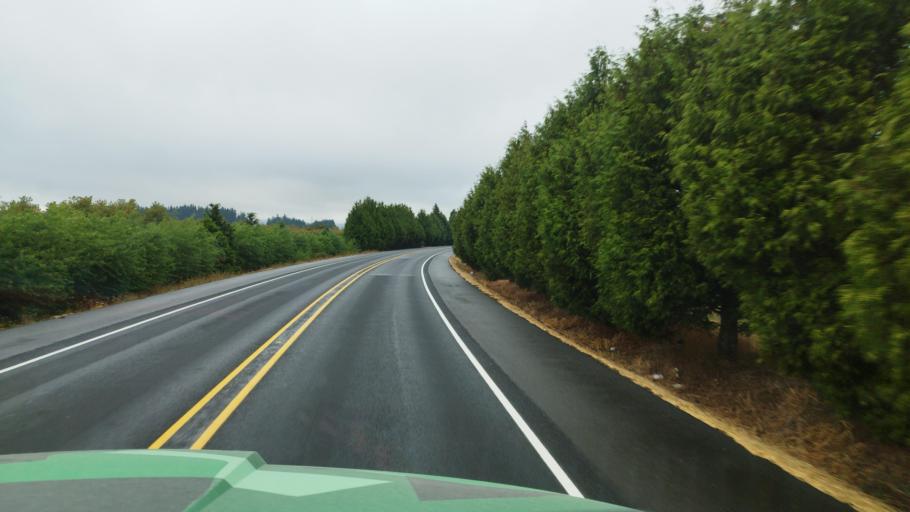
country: US
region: Oregon
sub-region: Washington County
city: Cornelius
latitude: 45.5404
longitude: -123.0737
